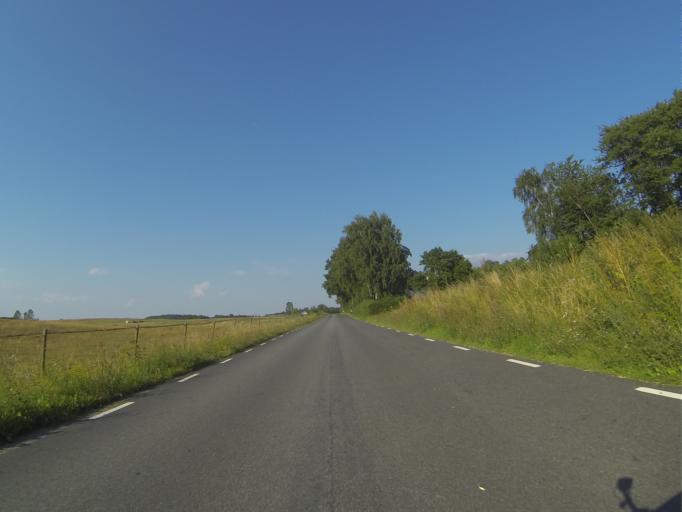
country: SE
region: Skane
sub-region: Lunds Kommun
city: Genarp
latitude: 55.5840
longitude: 13.3482
